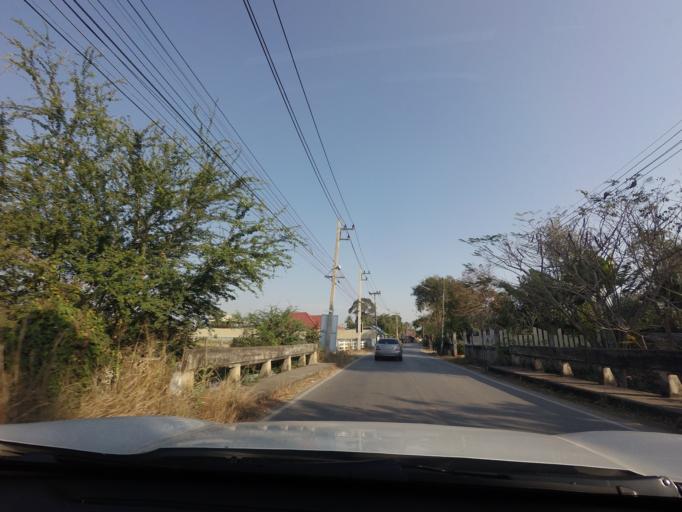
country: TH
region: Nakhon Ratchasima
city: Pak Chong
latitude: 14.6084
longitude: 101.4447
